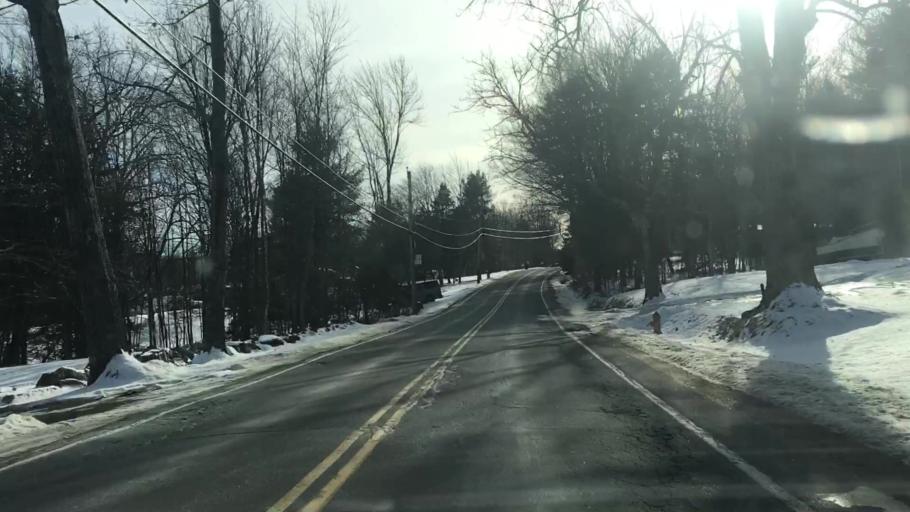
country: US
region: Maine
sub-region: Cumberland County
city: Westbrook
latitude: 43.7211
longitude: -70.3573
